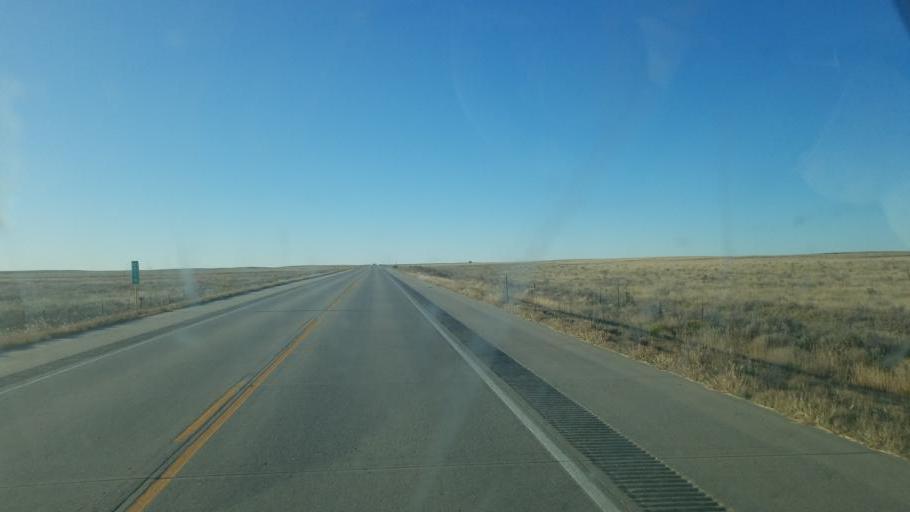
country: US
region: Colorado
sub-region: Kiowa County
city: Eads
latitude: 38.5606
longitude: -102.7861
